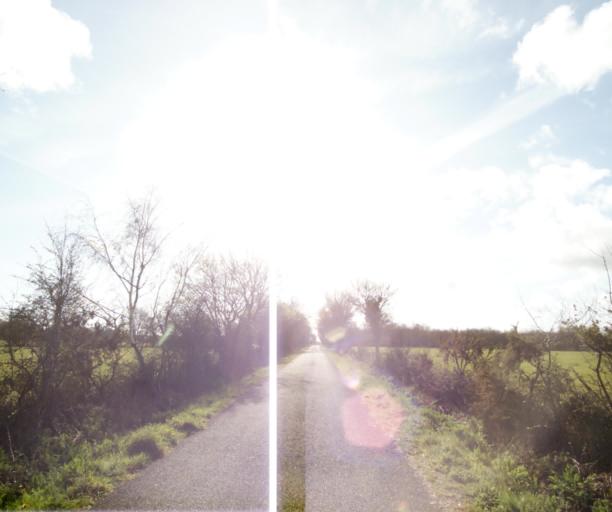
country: FR
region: Pays de la Loire
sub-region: Departement de la Loire-Atlantique
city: Bouvron
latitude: 47.4065
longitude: -1.8383
